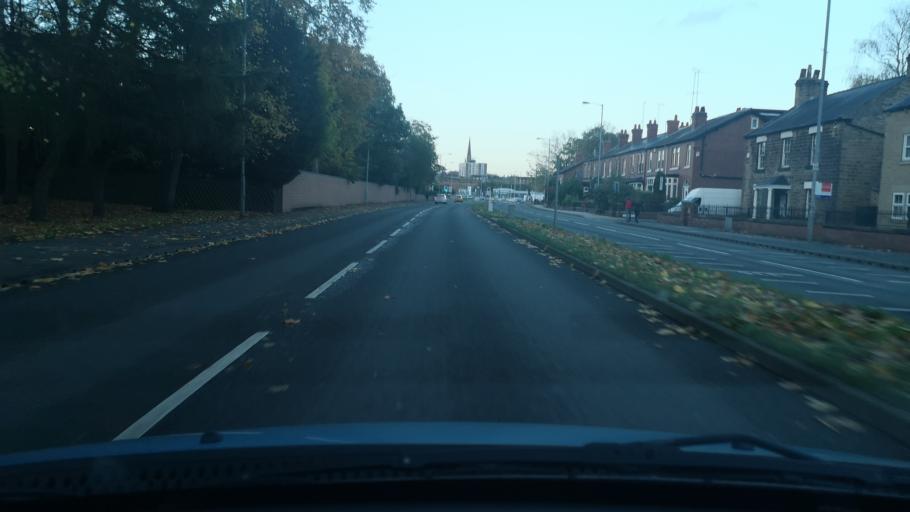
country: GB
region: England
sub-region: City and Borough of Wakefield
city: Wakefield
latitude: 53.6740
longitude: -1.5023
